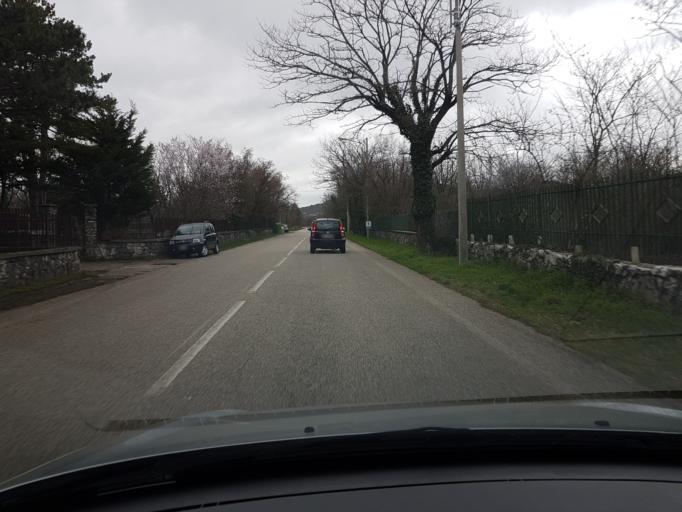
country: IT
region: Friuli Venezia Giulia
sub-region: Provincia di Trieste
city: Santa Croce
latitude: 45.7540
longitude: 13.7123
